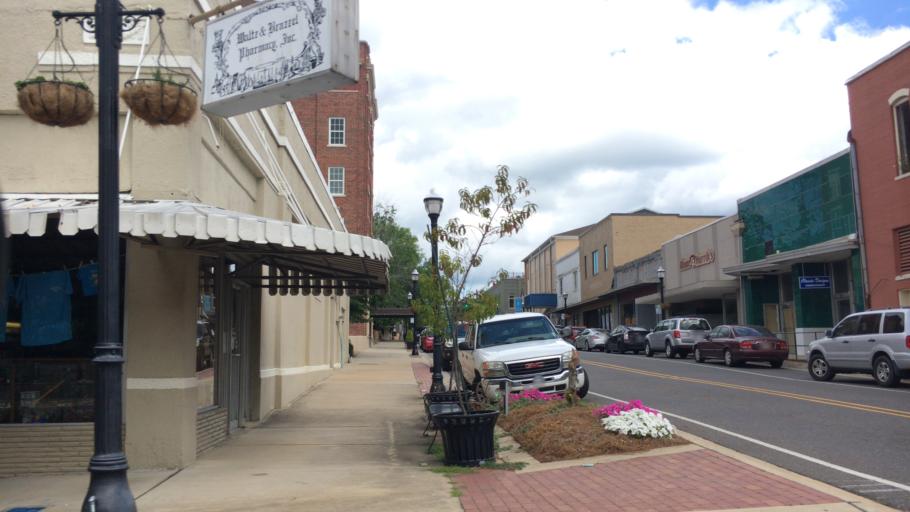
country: US
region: Louisiana
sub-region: Lincoln Parish
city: Ruston
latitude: 32.5300
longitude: -92.6392
